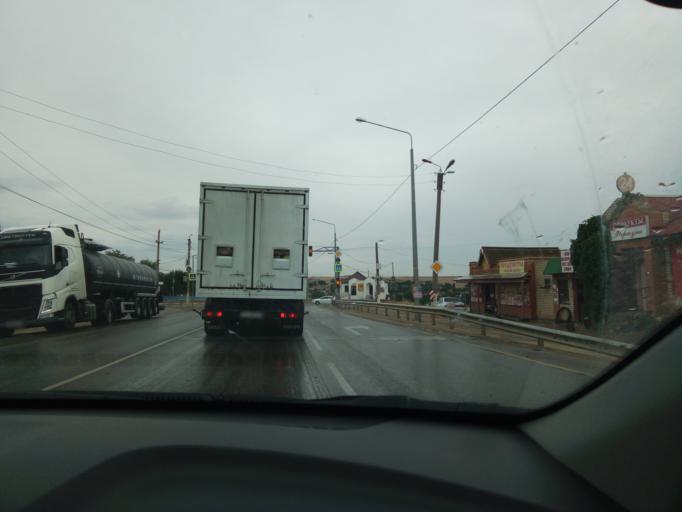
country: RU
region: Kalmykiya
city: Troitskoye
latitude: 46.4191
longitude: 44.2536
